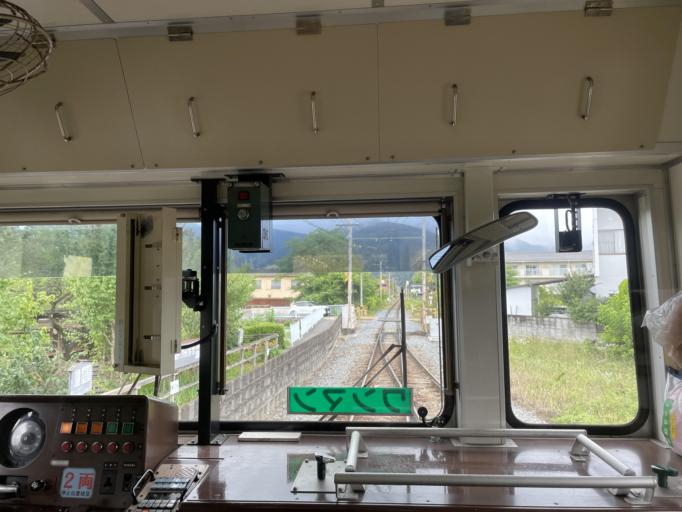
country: JP
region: Saitama
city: Kodamacho-kodamaminami
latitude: 36.1132
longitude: 139.1109
